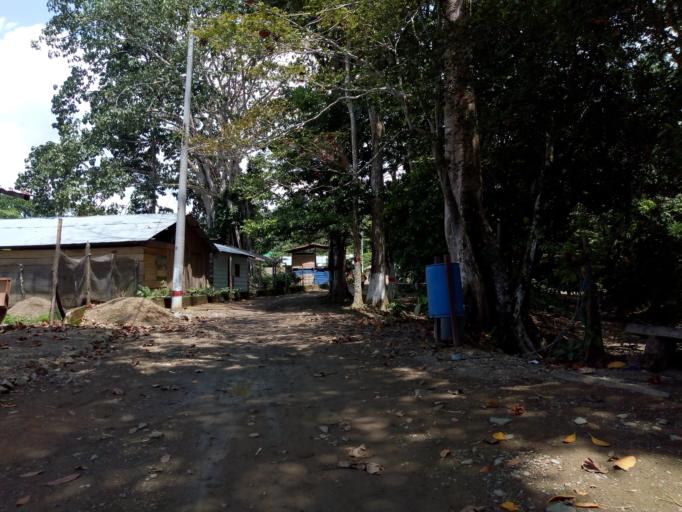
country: PA
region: Guna Yala
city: Puerto Obaldia
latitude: 8.6271
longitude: -77.3558
